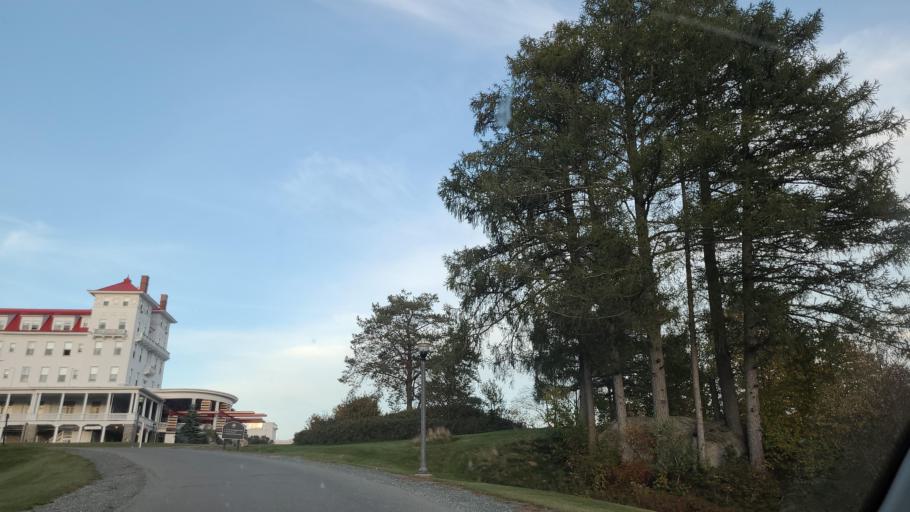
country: US
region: New Hampshire
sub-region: Coos County
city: Jefferson
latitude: 44.2562
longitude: -71.4405
